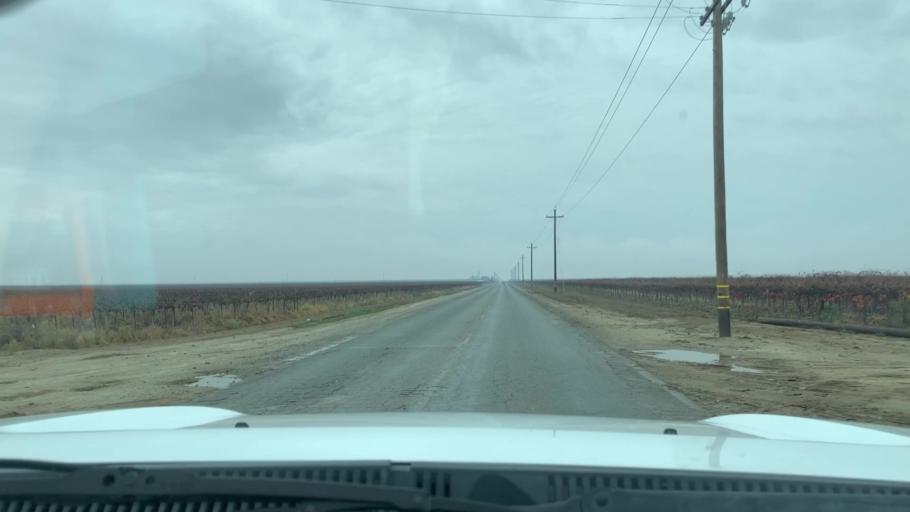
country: US
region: California
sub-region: Kern County
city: Delano
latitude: 35.7610
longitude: -119.3834
